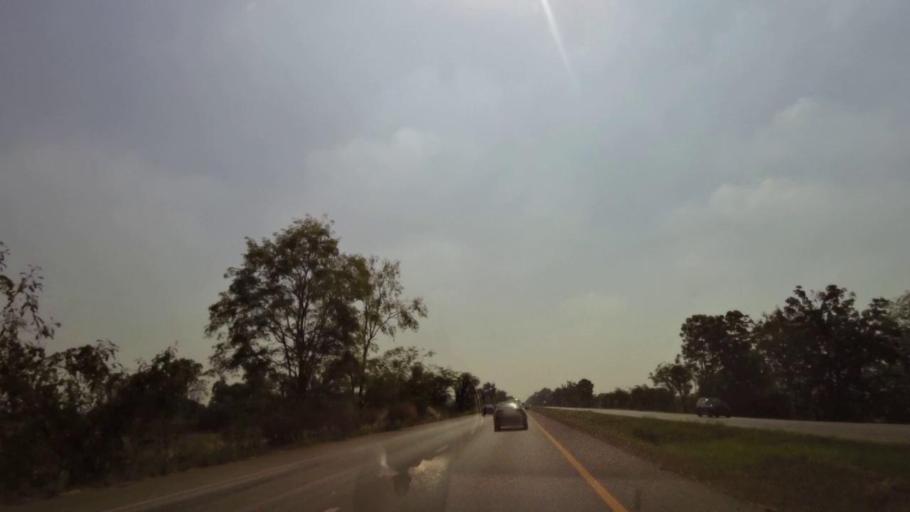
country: TH
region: Phichit
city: Wachira Barami
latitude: 16.4510
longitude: 100.1466
